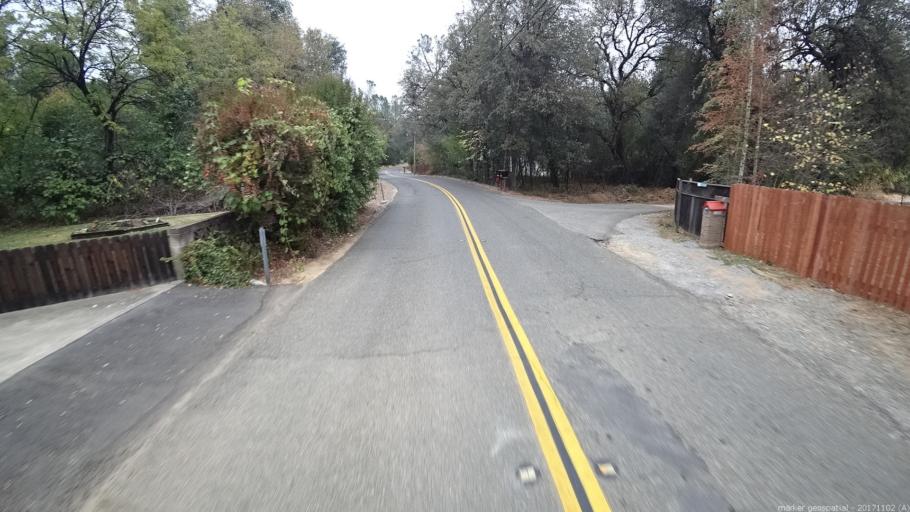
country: US
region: California
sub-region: Shasta County
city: Redding
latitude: 40.6334
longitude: -122.4159
